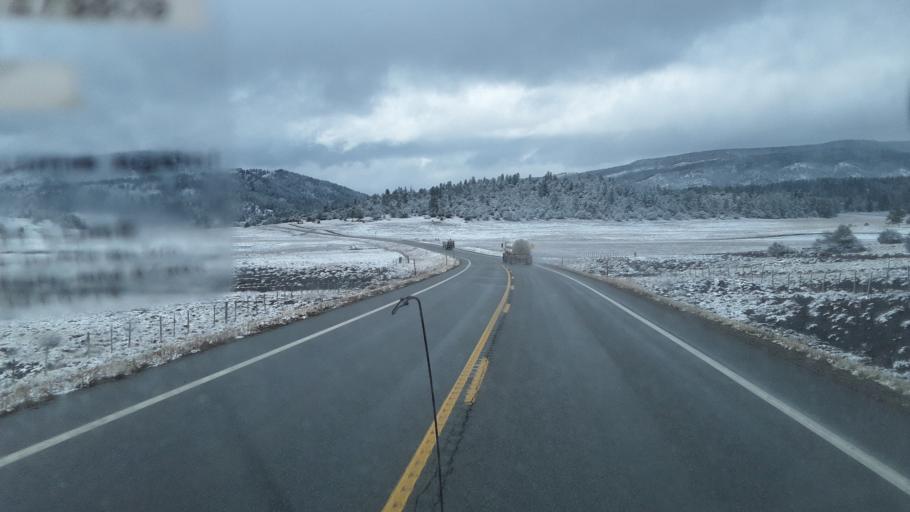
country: US
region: Colorado
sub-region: Archuleta County
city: Pagosa Springs
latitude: 37.2290
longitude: -107.1978
